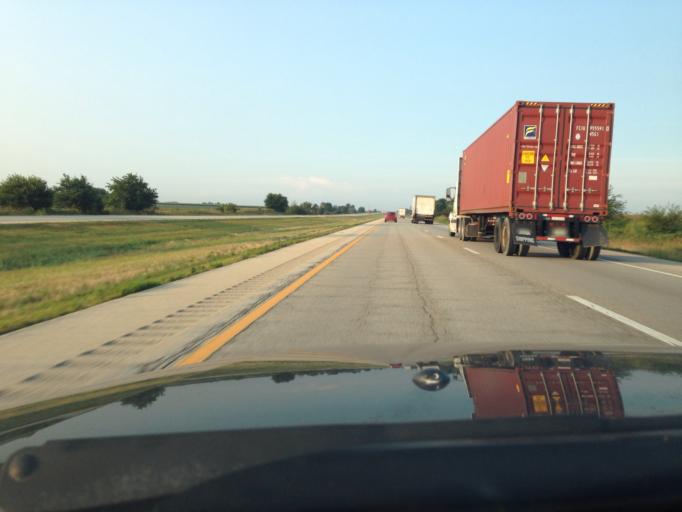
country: US
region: Illinois
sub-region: Ford County
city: Paxton
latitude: 40.5041
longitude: -88.0868
